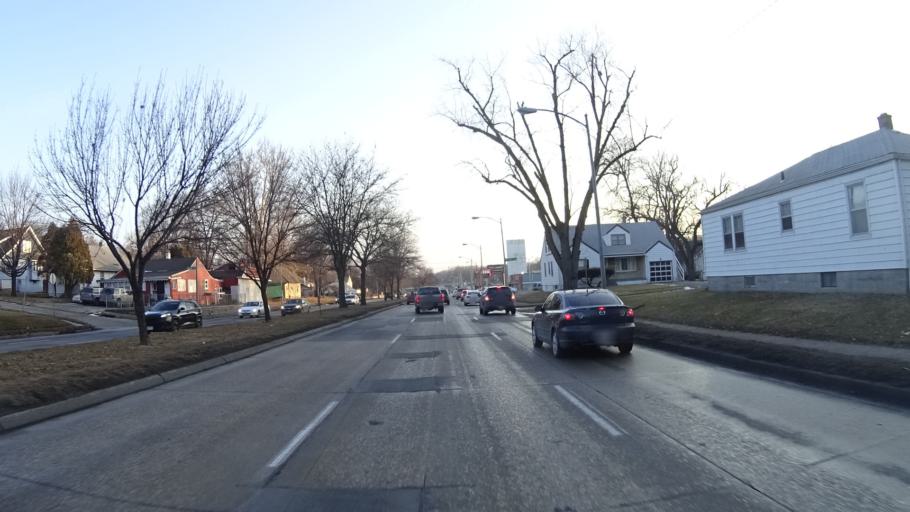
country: US
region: Nebraska
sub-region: Douglas County
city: Omaha
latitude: 41.2756
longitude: -95.9836
